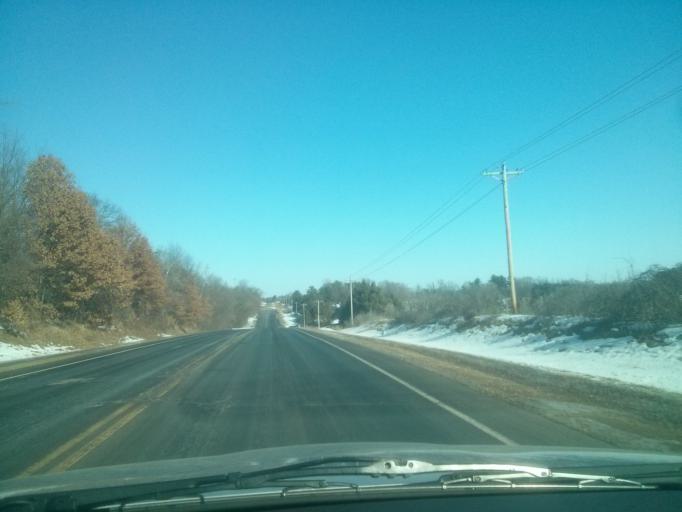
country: US
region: Minnesota
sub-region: Washington County
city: Stillwater
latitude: 45.0831
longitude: -92.7362
